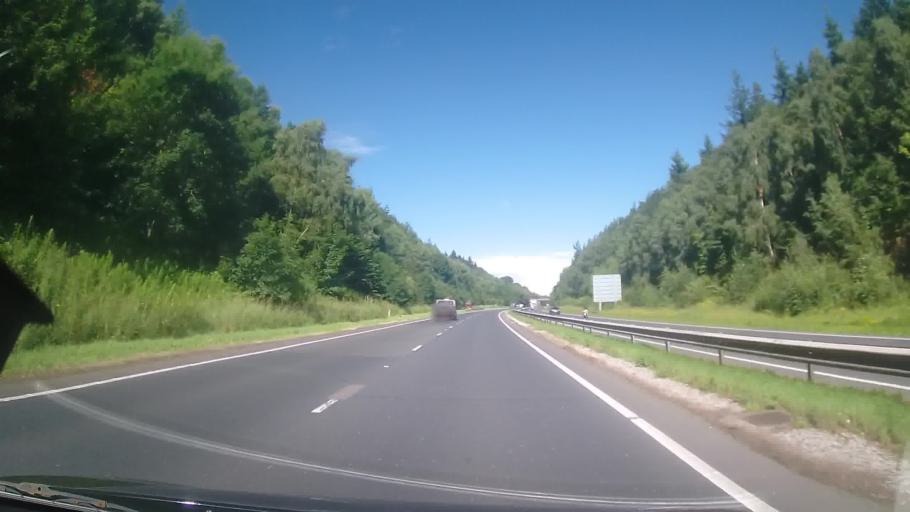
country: GB
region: Wales
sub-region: County of Flintshire
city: Hawarden
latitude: 53.1635
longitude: -3.0238
